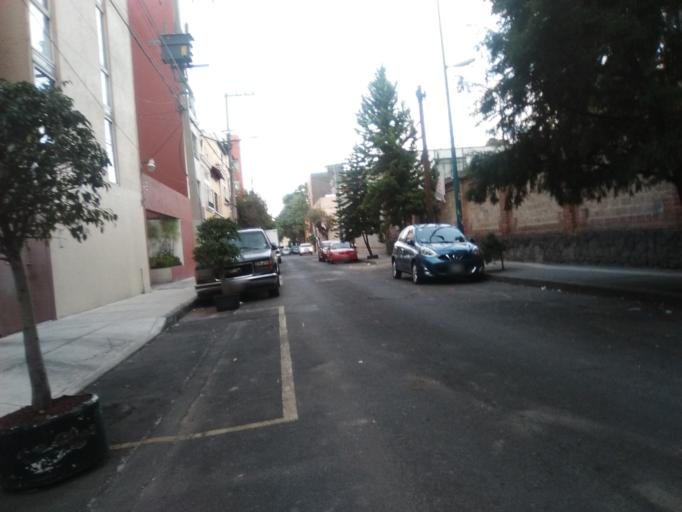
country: MX
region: Mexico City
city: Alvaro Obregon
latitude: 19.3761
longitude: -99.1854
